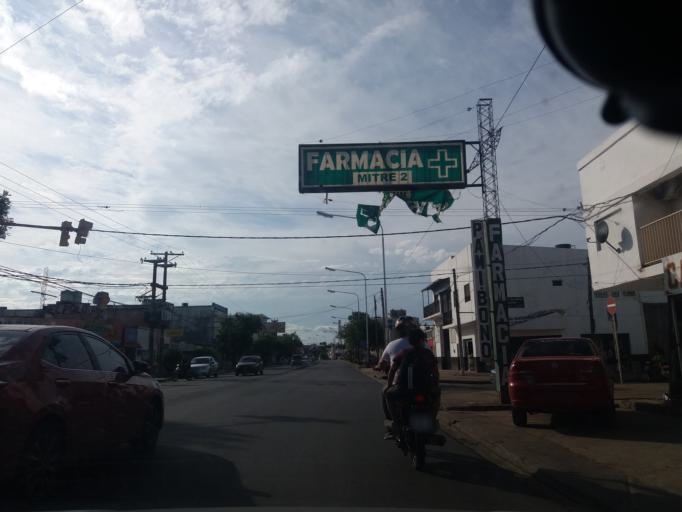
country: AR
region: Corrientes
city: Corrientes
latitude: -27.4914
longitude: -58.8197
